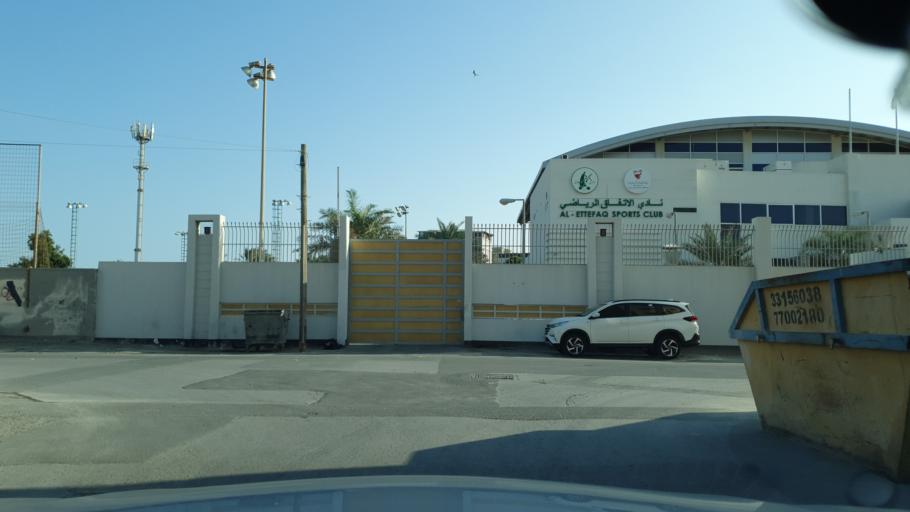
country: BH
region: Manama
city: Jidd Hafs
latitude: 26.2218
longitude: 50.4623
